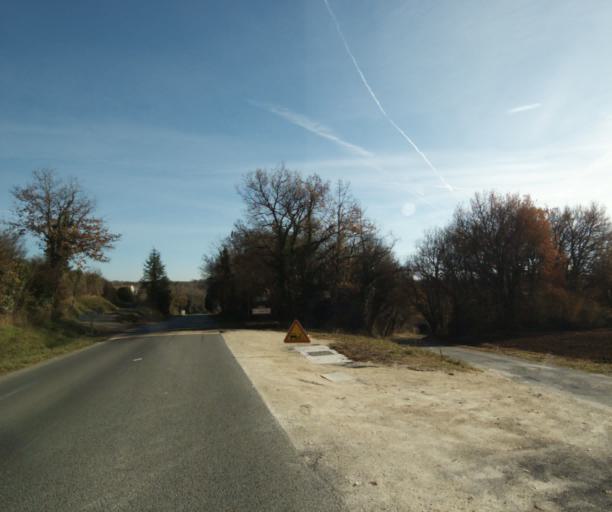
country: FR
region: Poitou-Charentes
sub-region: Departement de la Charente-Maritime
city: Chaniers
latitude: 45.7521
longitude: -0.5128
